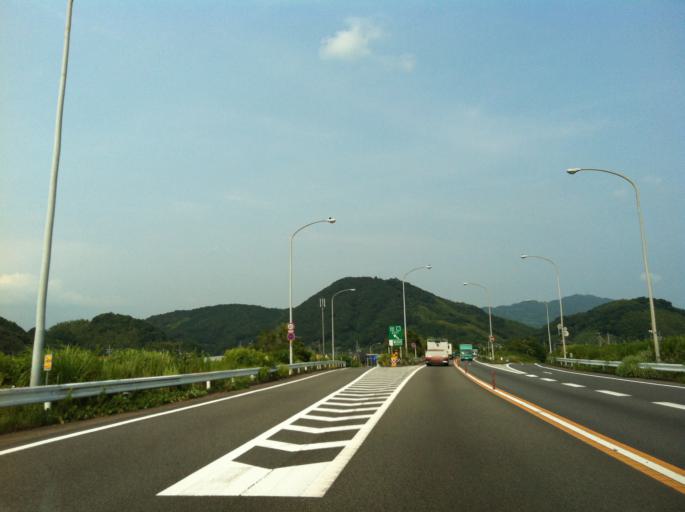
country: JP
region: Shizuoka
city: Fujieda
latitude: 34.8885
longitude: 138.2539
